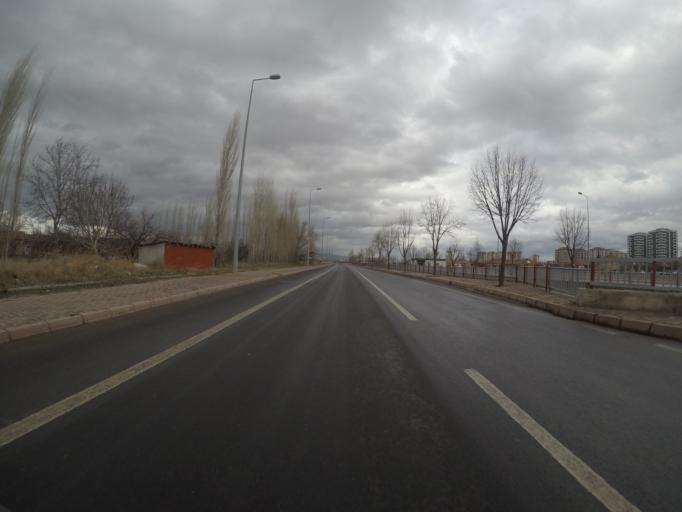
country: TR
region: Kayseri
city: Kayseri
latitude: 38.7524
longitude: 35.4762
